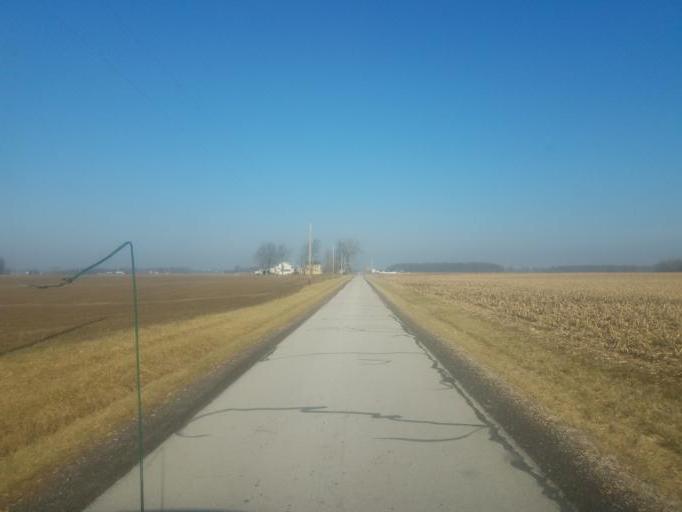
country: US
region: Ohio
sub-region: Seneca County
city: Tiffin
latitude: 41.0376
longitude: -83.1130
